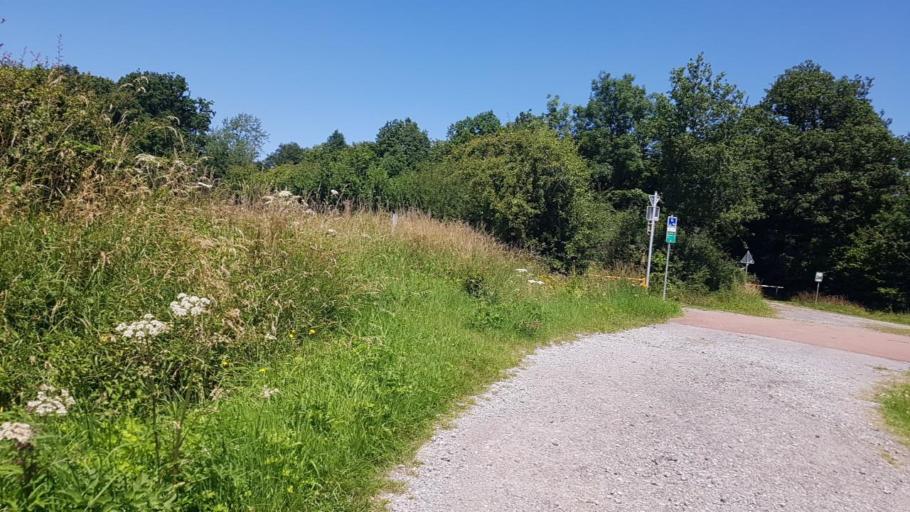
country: BE
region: Wallonia
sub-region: Province du Hainaut
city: Froidchapelle
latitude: 50.1512
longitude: 4.2732
